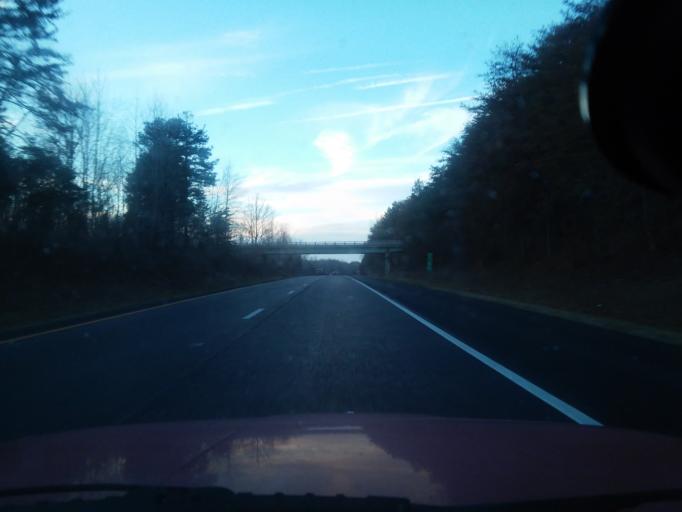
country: US
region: Virginia
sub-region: Louisa County
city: Louisa
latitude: 37.8839
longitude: -78.0303
